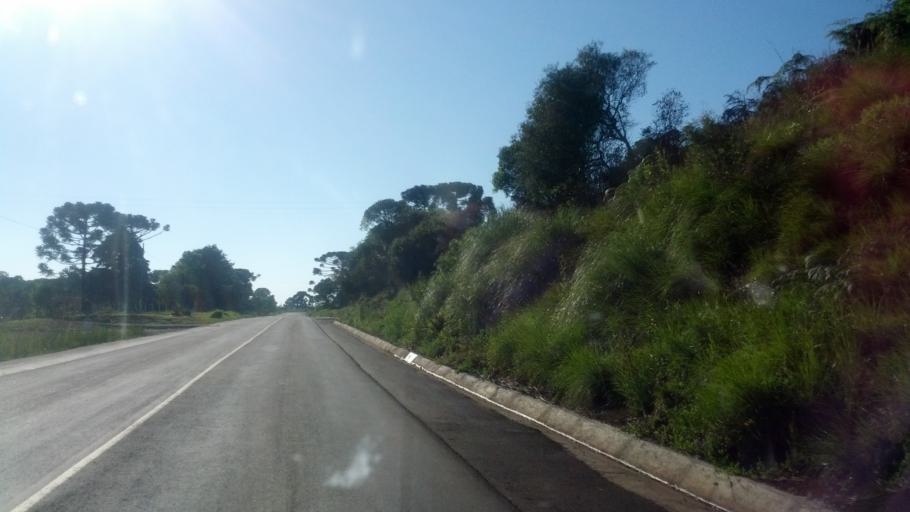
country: BR
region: Santa Catarina
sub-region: Lages
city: Lages
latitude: -27.9294
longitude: -50.5333
